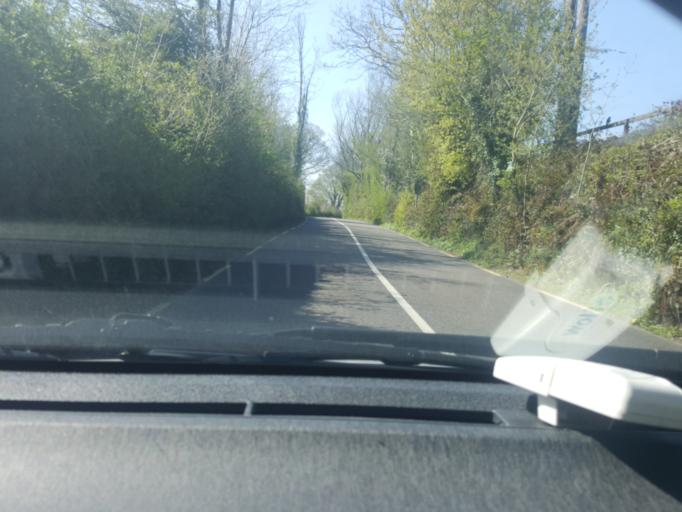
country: IE
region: Munster
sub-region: County Cork
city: Bandon
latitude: 51.7621
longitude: -8.6489
